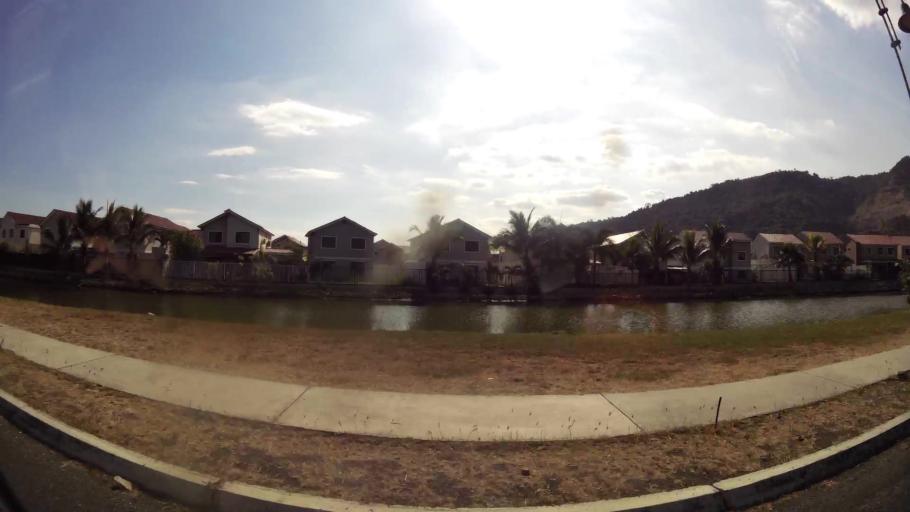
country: EC
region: Guayas
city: Santa Lucia
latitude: -2.1883
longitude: -80.0012
